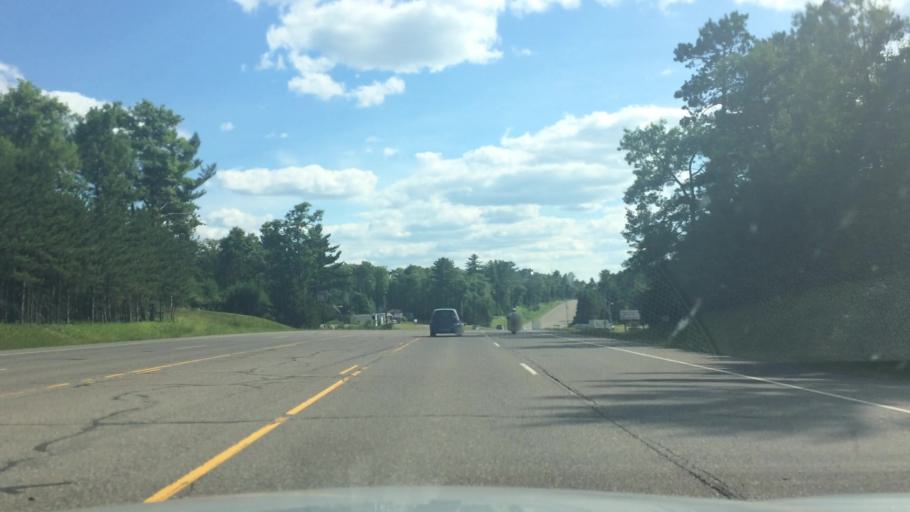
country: US
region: Wisconsin
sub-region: Vilas County
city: Lac du Flambeau
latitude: 45.8402
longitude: -89.7078
